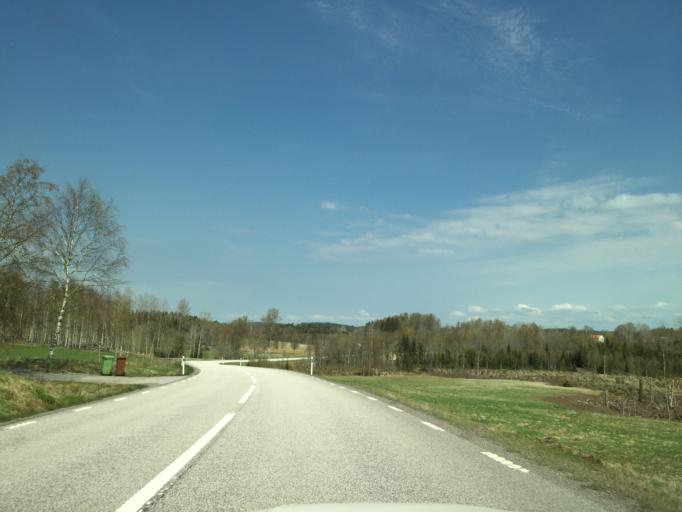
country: SE
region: Vaestra Goetaland
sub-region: Bengtsfors Kommun
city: Dals Langed
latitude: 58.8594
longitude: 12.1846
